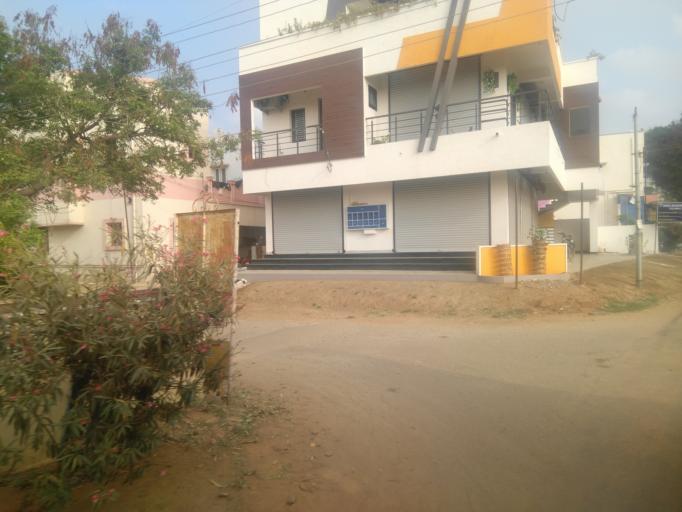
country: IN
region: Tamil Nadu
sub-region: Coimbatore
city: Coimbatore
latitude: 11.0625
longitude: 76.9058
